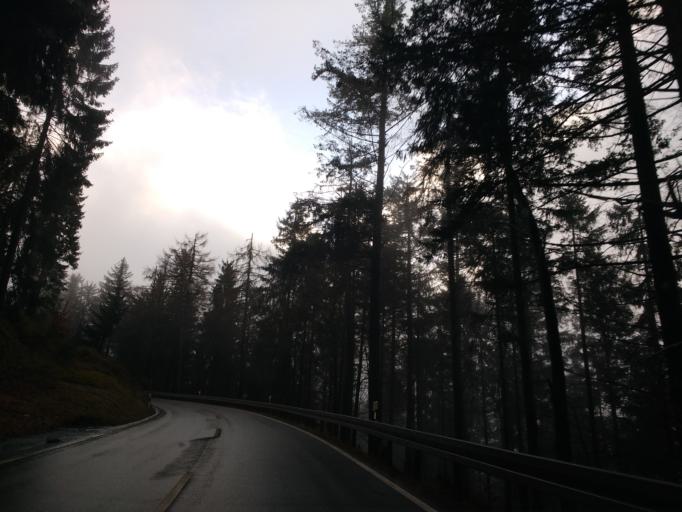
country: DE
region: Baden-Wuerttemberg
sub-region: Freiburg Region
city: Seebach
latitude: 48.5755
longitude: 8.2121
